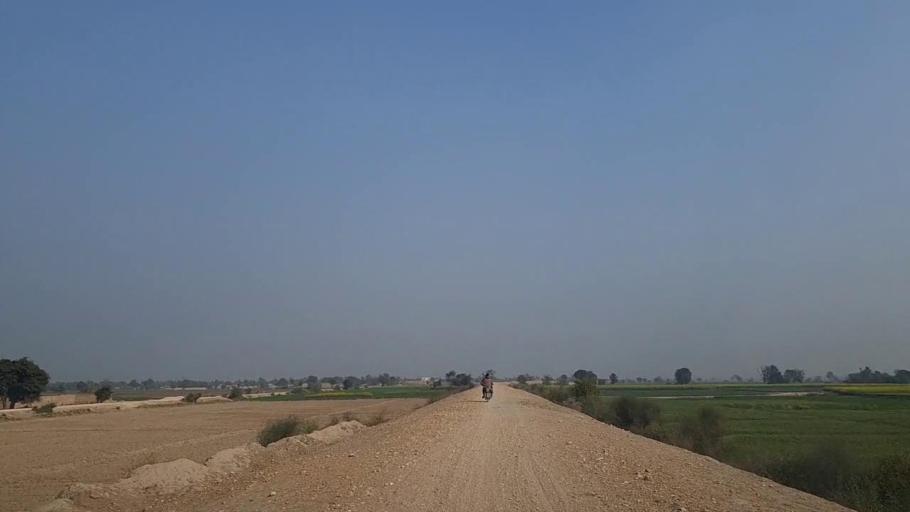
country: PK
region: Sindh
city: Sann
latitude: 26.0840
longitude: 68.1735
